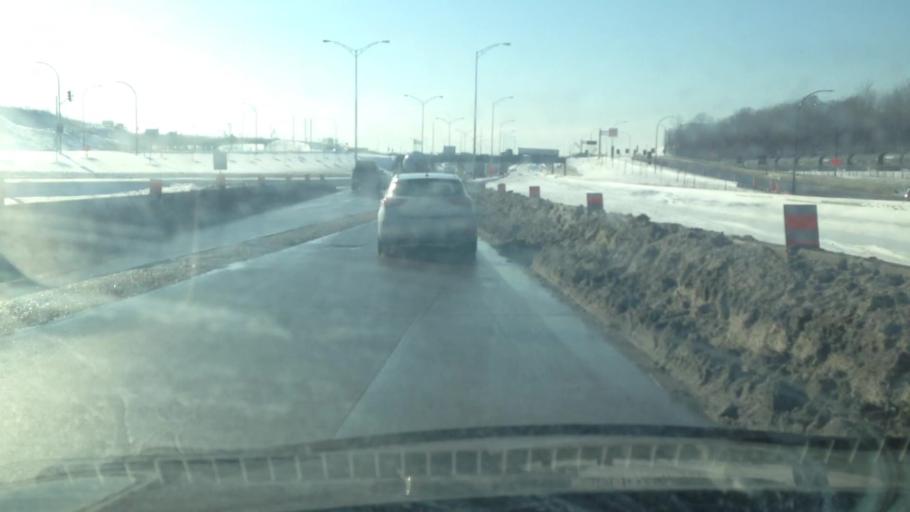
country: CA
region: Quebec
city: Saint-Raymond
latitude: 45.4569
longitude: -73.6238
